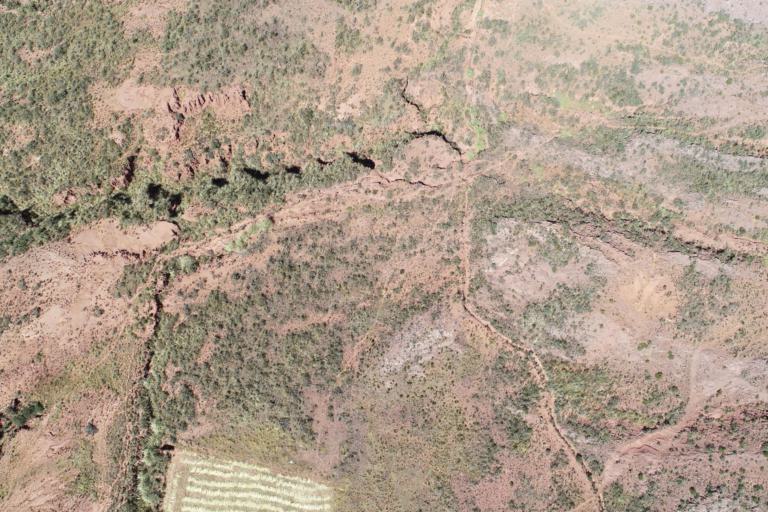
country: BO
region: La Paz
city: Tiahuanaco
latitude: -16.5979
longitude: -68.7556
